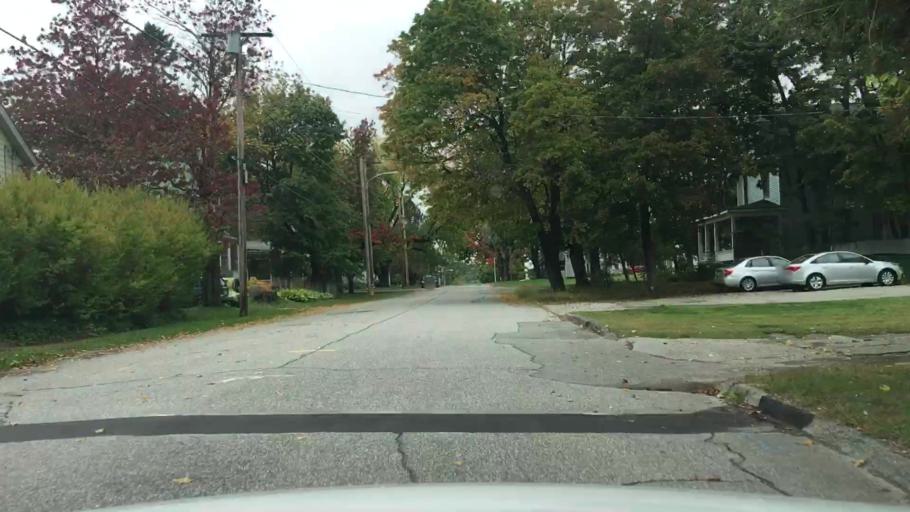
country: US
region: Maine
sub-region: Kennebec County
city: Waterville
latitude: 44.5591
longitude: -69.6356
